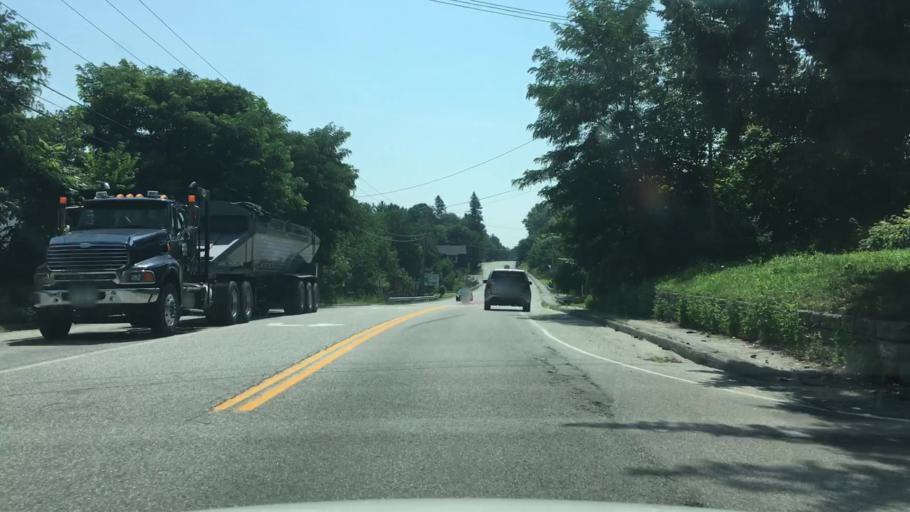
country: US
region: Maine
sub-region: Kennebec County
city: Hallowell
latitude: 44.2681
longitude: -69.7876
